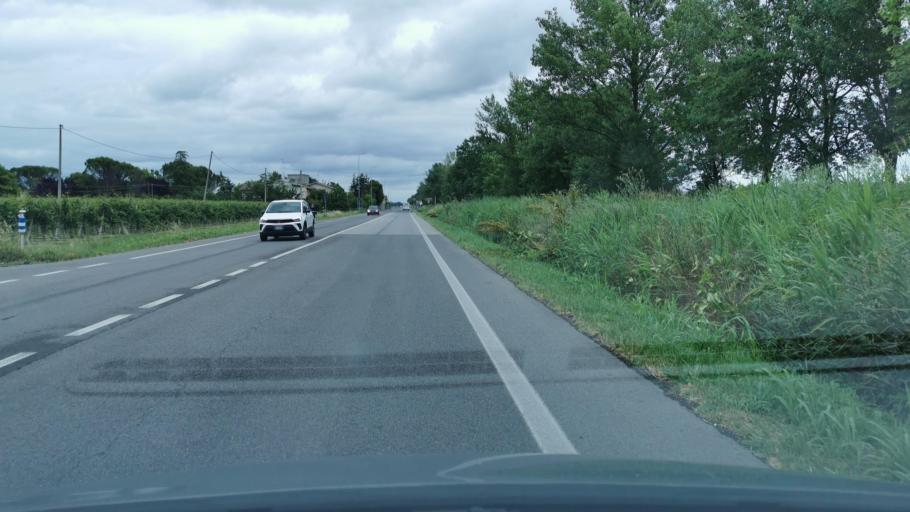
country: IT
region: Emilia-Romagna
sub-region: Provincia di Ravenna
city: Granarolo
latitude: 44.3289
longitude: 11.9108
